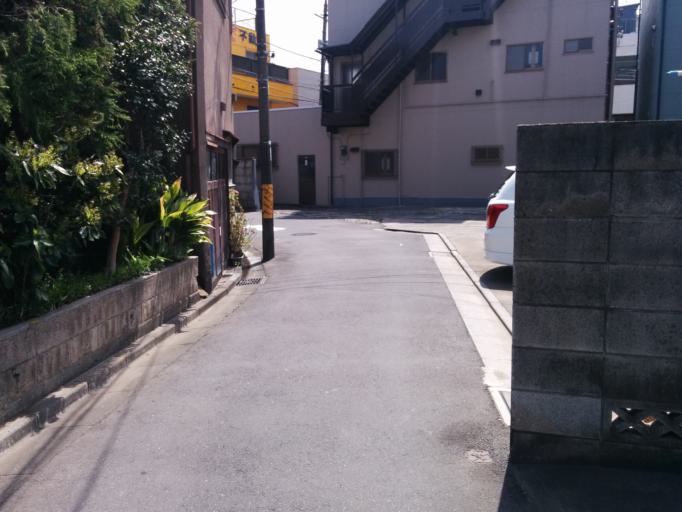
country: JP
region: Tokyo
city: Urayasu
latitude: 35.7231
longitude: 139.8274
